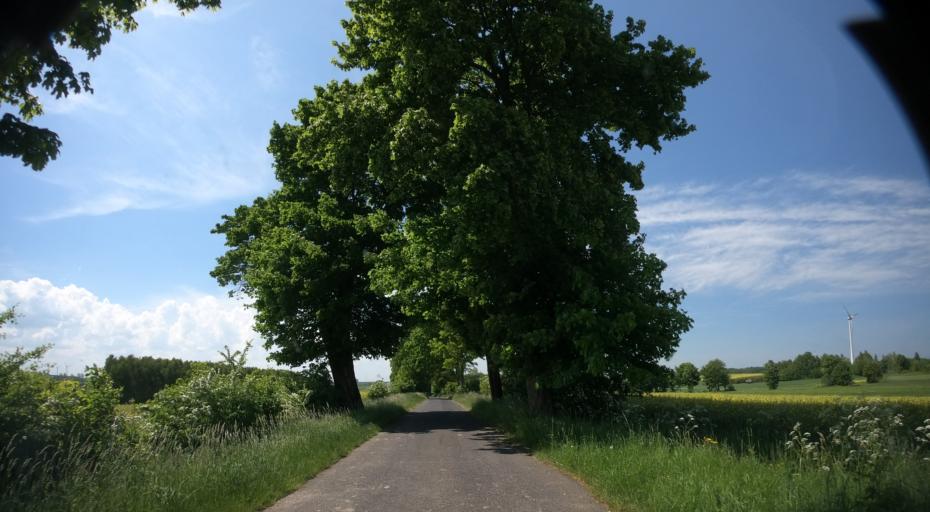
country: PL
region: West Pomeranian Voivodeship
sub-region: Powiat kolobrzeski
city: Ustronie Morskie
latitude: 54.1589
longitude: 15.8058
